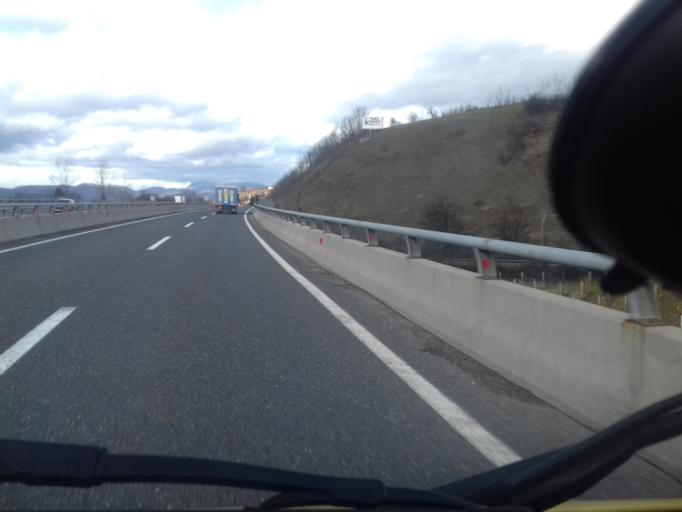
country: BA
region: Federation of Bosnia and Herzegovina
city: Visoko
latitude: 43.9919
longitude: 18.1965
